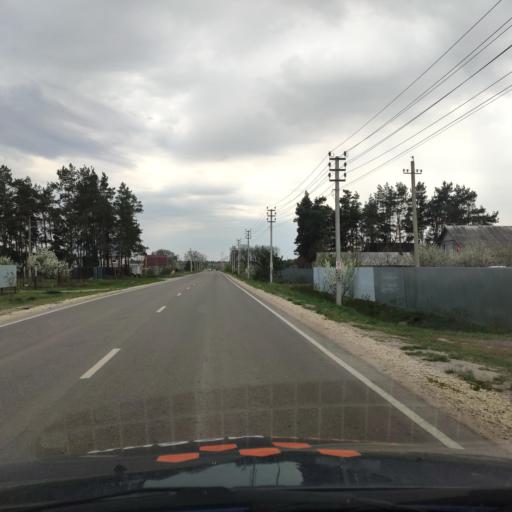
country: RU
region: Voronezj
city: Podgornoye
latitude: 51.8774
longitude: 39.1731
